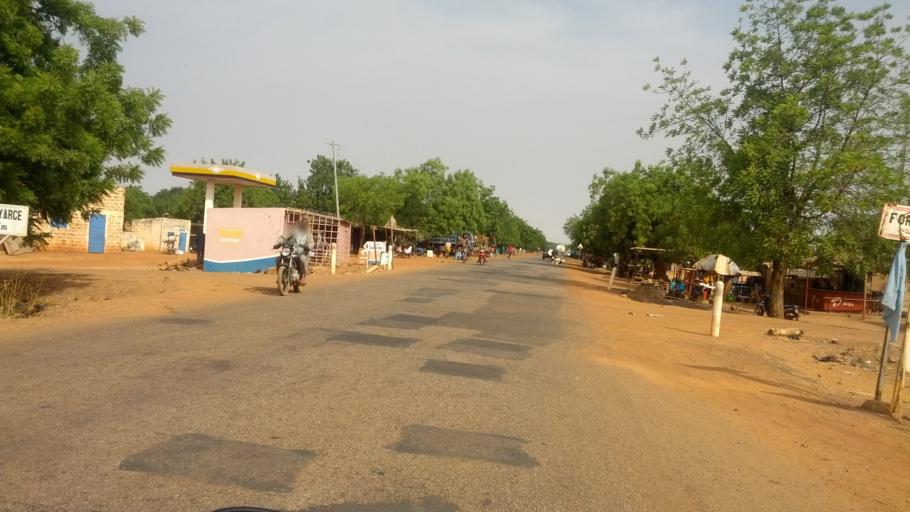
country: BF
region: Centre-Nord
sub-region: Province du Sanmatenga
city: Kaya
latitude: 12.9093
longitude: -1.0782
